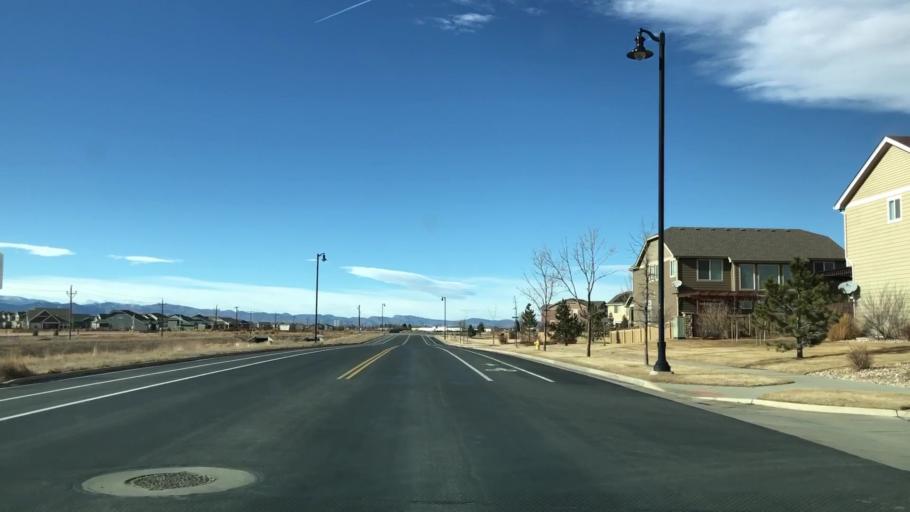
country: US
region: Colorado
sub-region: Weld County
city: Windsor
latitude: 40.5099
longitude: -104.9506
